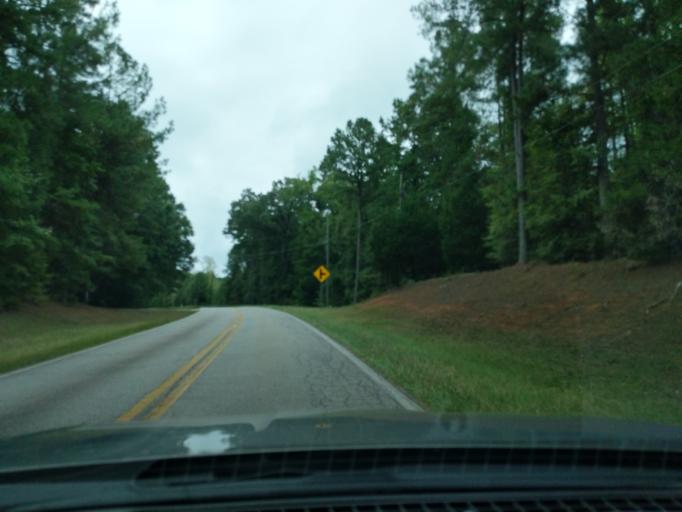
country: US
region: Georgia
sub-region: Columbia County
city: Appling
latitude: 33.5678
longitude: -82.3663
